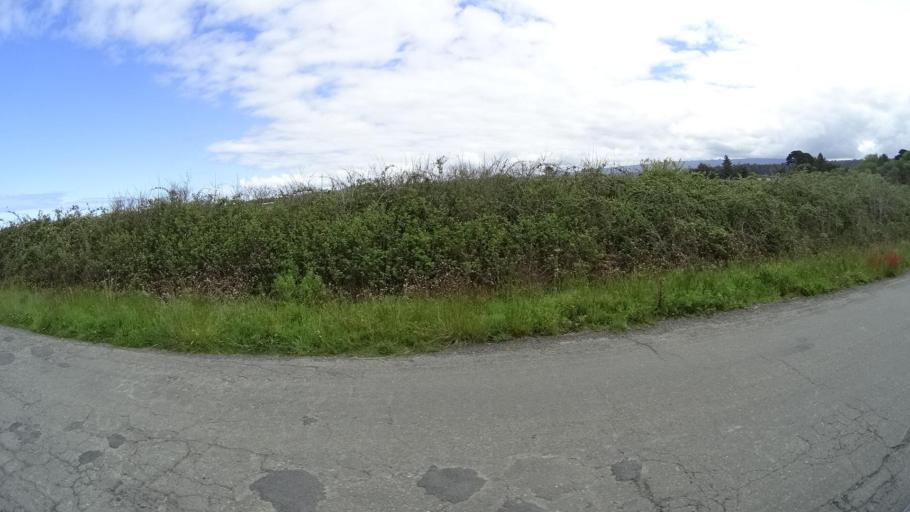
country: US
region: California
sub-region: Humboldt County
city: Arcata
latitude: 40.8804
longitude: -124.0979
